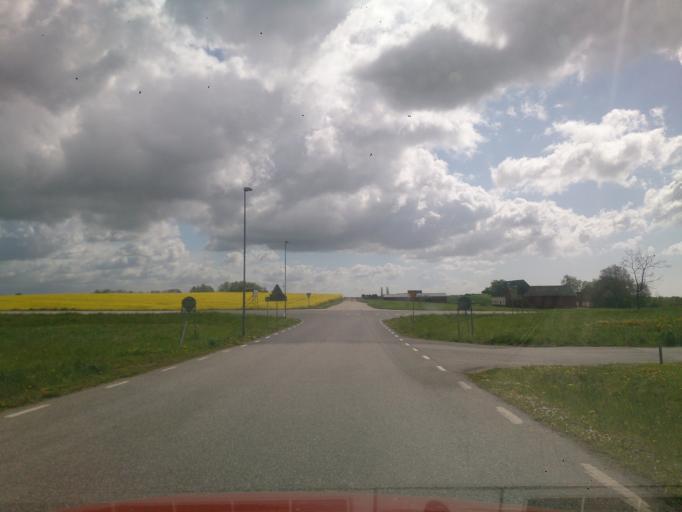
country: SE
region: Skane
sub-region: Ystads Kommun
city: Ystad
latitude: 55.4347
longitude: 13.7181
